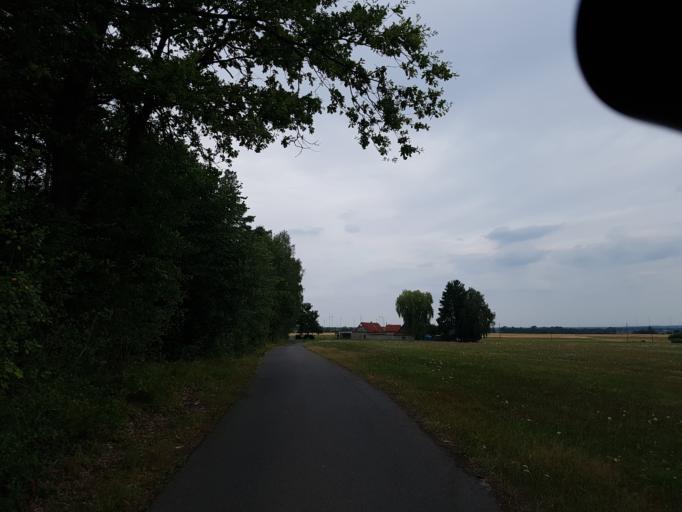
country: DE
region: Brandenburg
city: Sallgast
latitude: 51.5809
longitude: 13.8578
